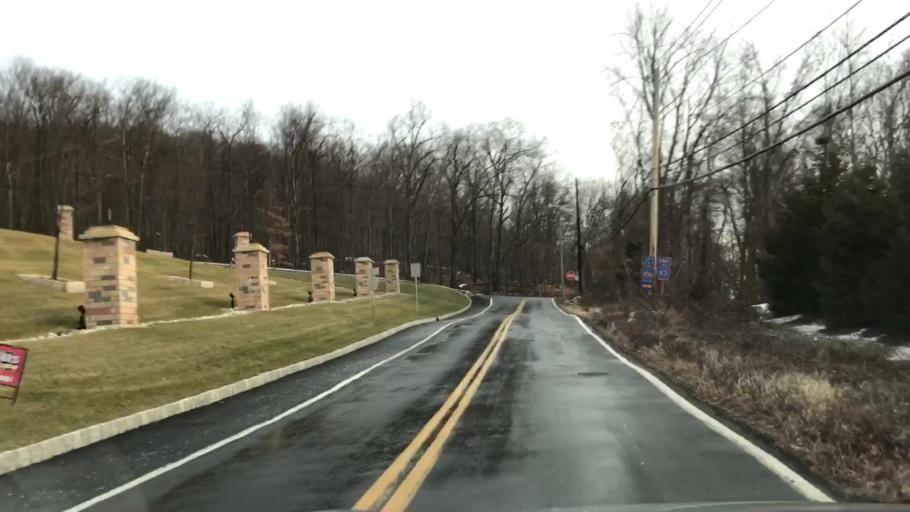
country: US
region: New York
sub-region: Rockland County
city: Thiells
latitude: 41.2308
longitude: -74.0445
